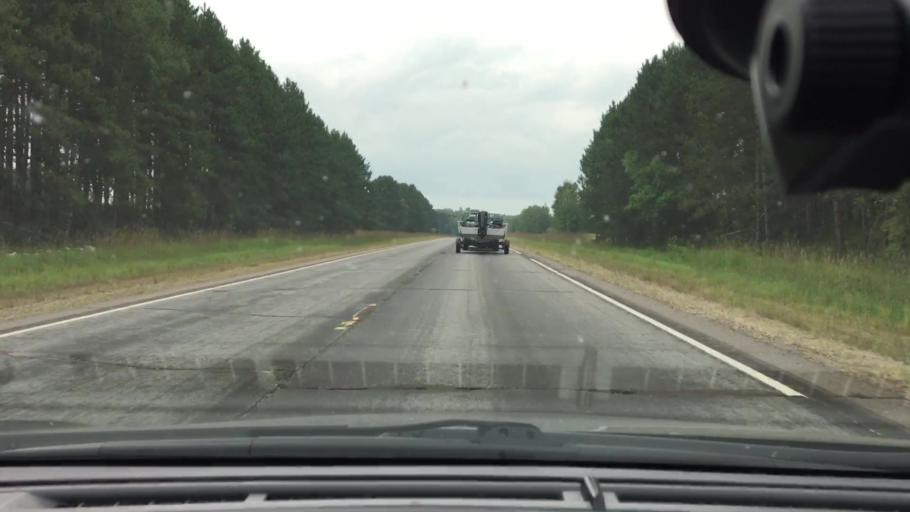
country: US
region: Minnesota
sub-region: Crow Wing County
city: Crosby
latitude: 46.6352
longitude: -93.9486
